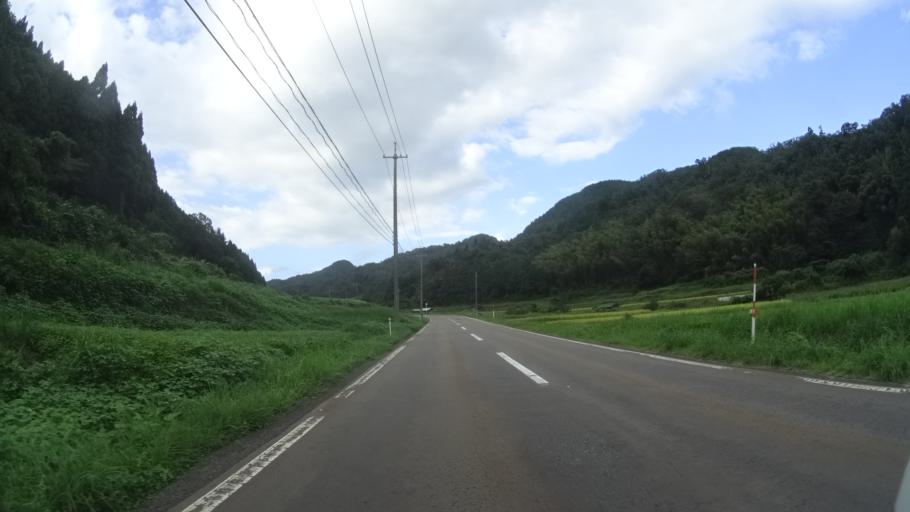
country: JP
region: Tottori
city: Kurayoshi
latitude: 35.4136
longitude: 133.9186
